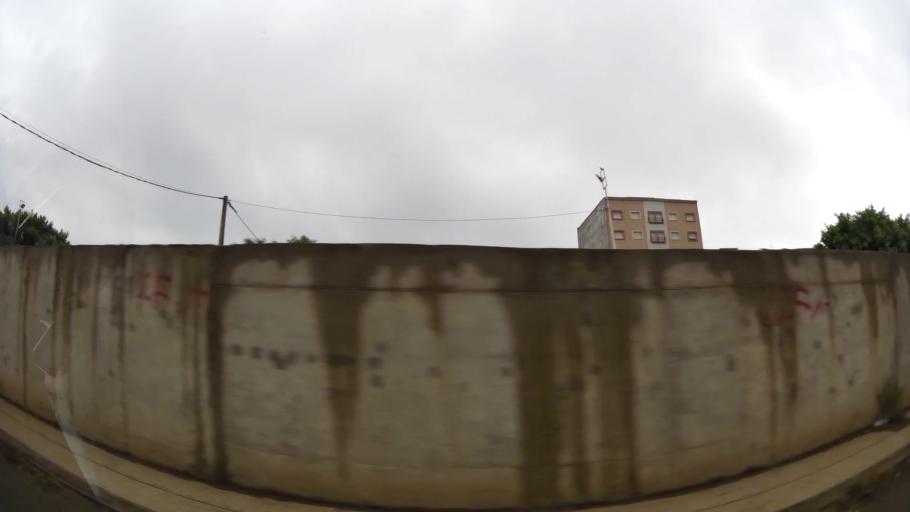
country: MA
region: Oriental
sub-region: Nador
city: Nador
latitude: 35.1644
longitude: -2.9560
